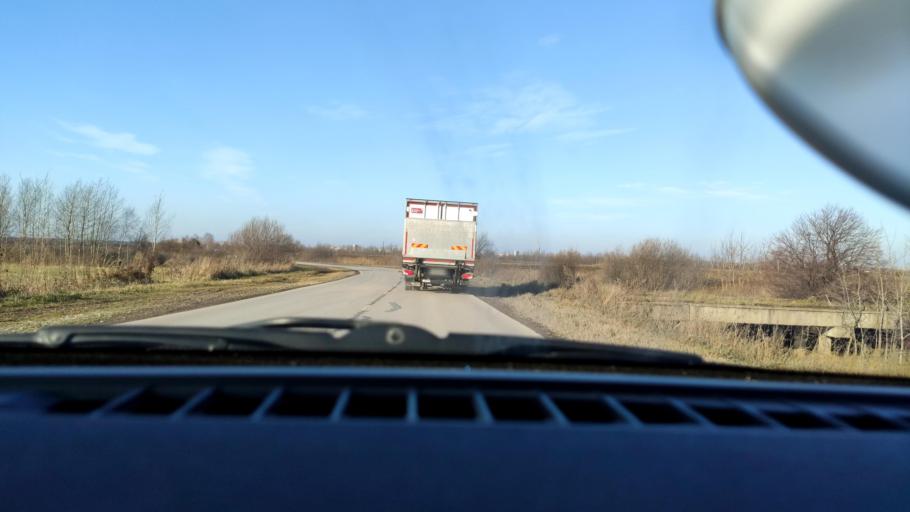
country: RU
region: Perm
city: Kondratovo
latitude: 57.9958
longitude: 56.0863
